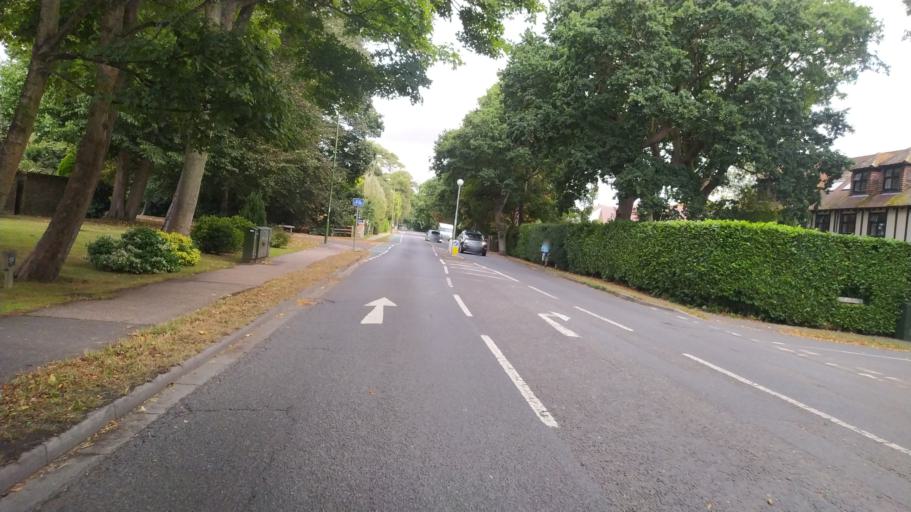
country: GB
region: England
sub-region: West Sussex
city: Chichester
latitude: 50.8548
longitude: -0.7821
